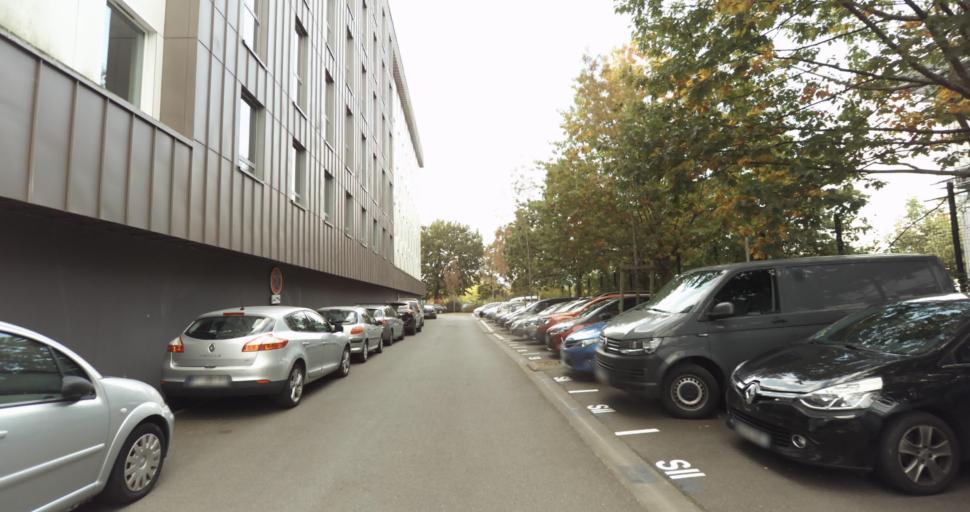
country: FR
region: Brittany
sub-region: Departement d'Ille-et-Vilaine
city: Cesson-Sevigne
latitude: 48.1291
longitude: -1.6250
